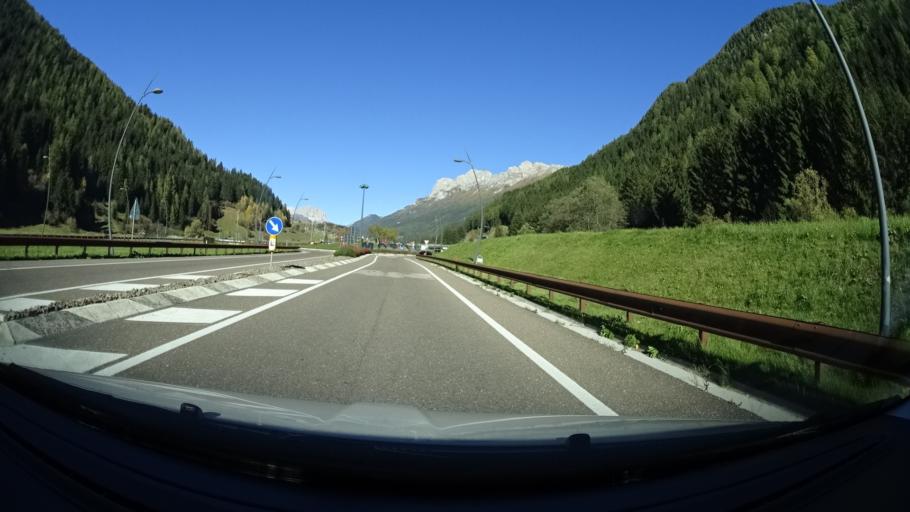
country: IT
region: Trentino-Alto Adige
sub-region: Provincia di Trento
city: Moena
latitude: 46.3625
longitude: 11.6460
